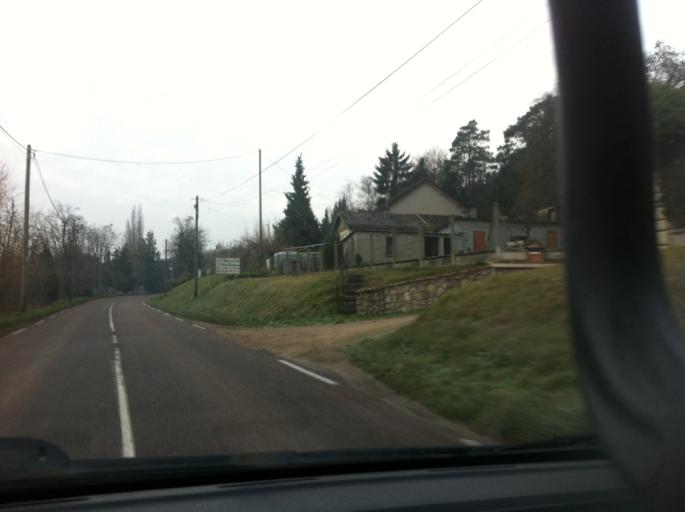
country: FR
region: Ile-de-France
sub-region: Departement de l'Essonne
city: Etampes
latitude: 48.4085
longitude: 2.1422
